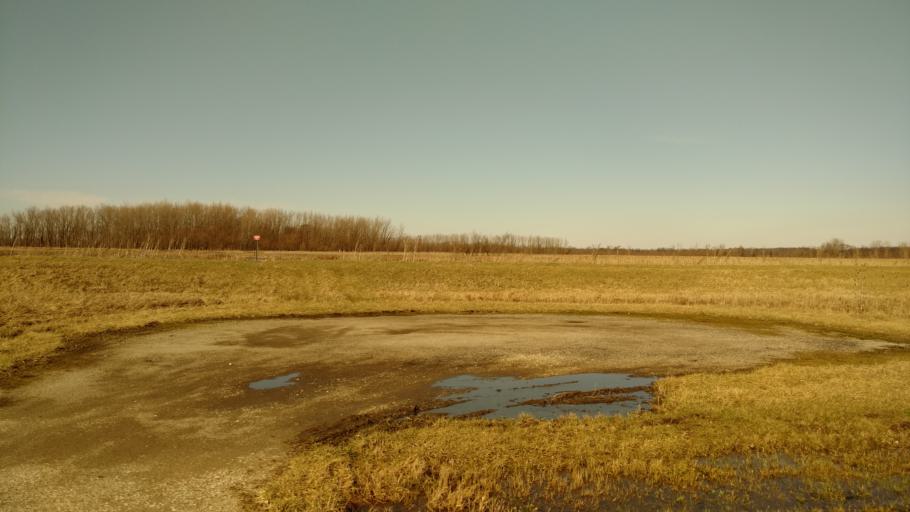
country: US
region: Ohio
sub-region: Wyandot County
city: Upper Sandusky
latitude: 40.7021
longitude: -83.2880
